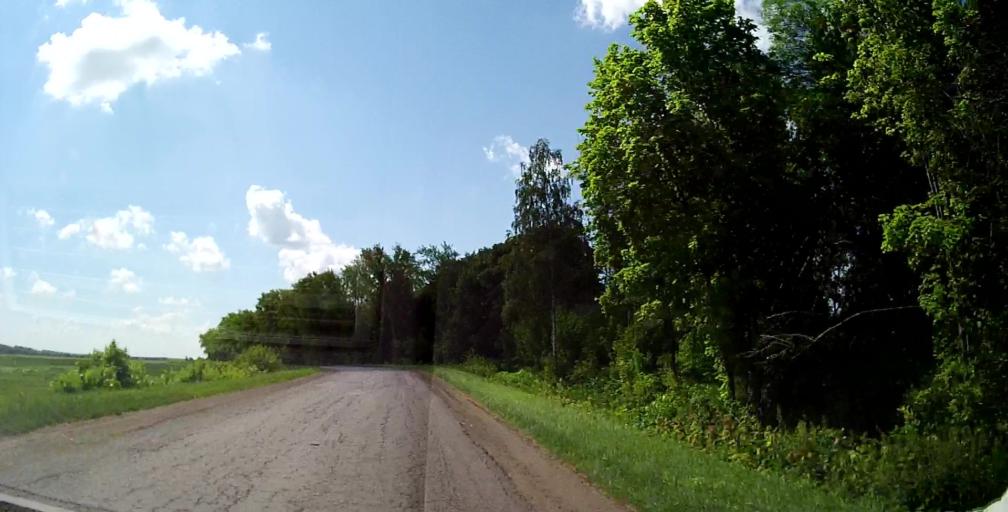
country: RU
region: Lipetsk
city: Chaplygin
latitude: 53.3009
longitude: 39.9519
